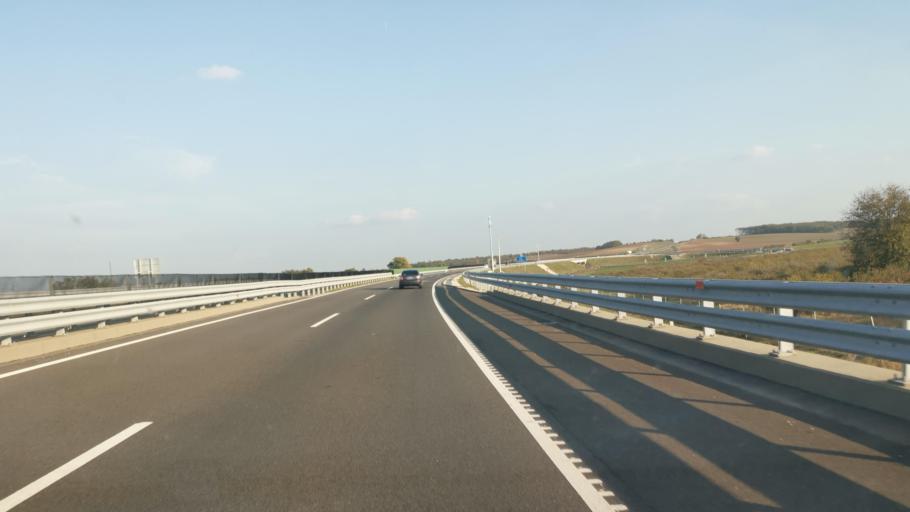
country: HU
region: Gyor-Moson-Sopron
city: Fertoszentmiklos
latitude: 47.5686
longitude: 16.8521
